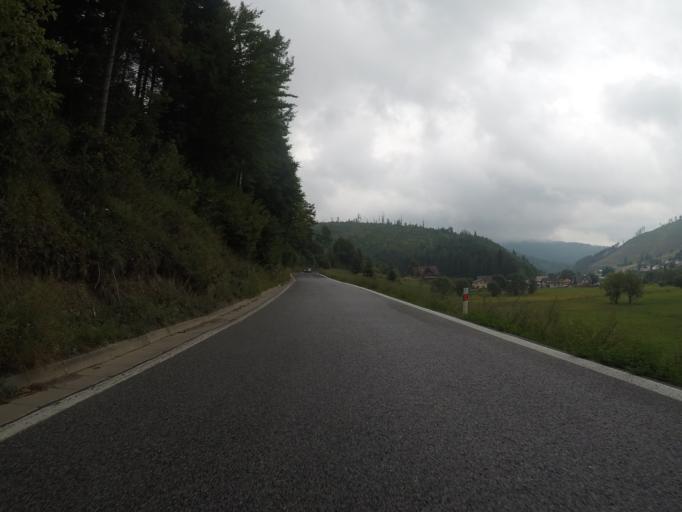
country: SK
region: Kosicky
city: Dobsina
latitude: 48.8559
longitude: 20.3951
